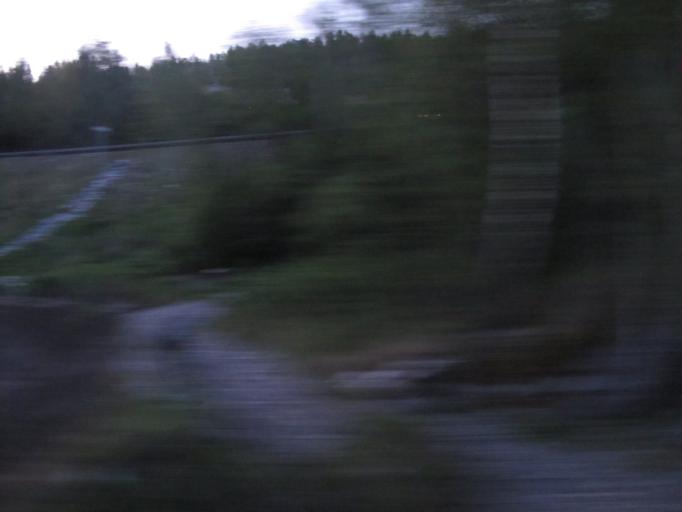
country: NO
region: Oppland
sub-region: Nord-Fron
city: Vinstra
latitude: 61.6343
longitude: 9.7190
